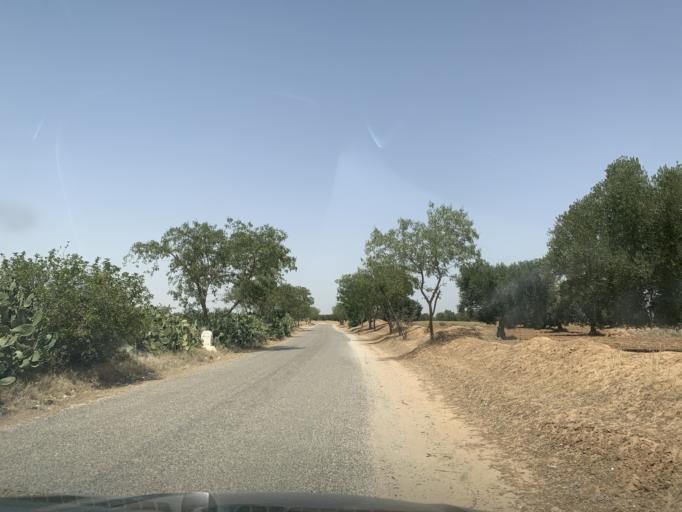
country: TN
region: Al Mahdiyah
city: Shurban
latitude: 35.1836
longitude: 10.2408
